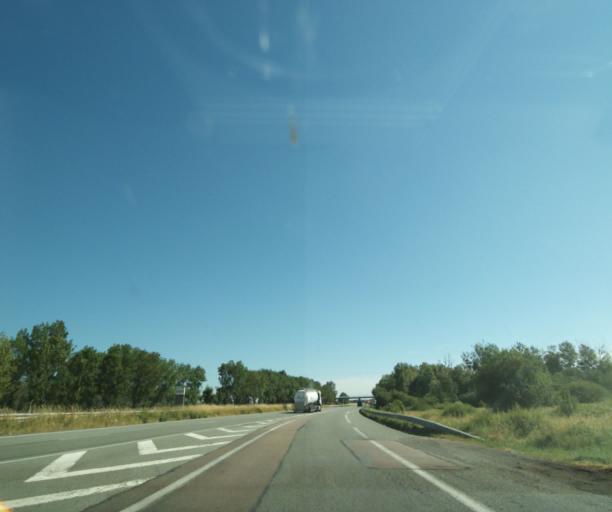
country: FR
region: Champagne-Ardenne
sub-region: Departement de la Haute-Marne
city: Avrecourt
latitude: 47.9772
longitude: 5.4993
